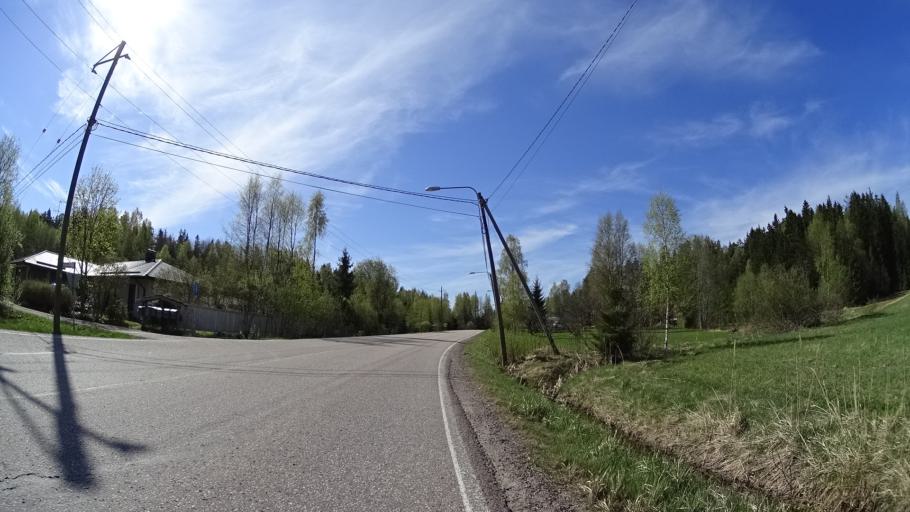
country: FI
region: Uusimaa
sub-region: Helsinki
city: Nurmijaervi
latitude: 60.3791
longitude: 24.8396
